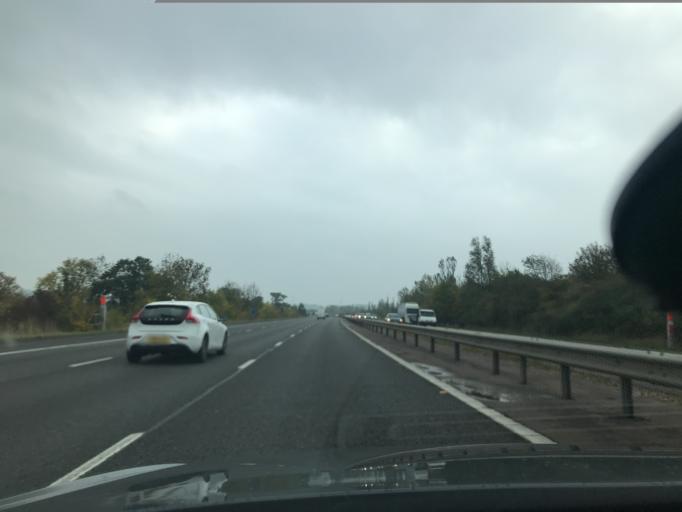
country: GB
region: England
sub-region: Oxfordshire
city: Bicester
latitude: 51.8386
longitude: -1.1358
